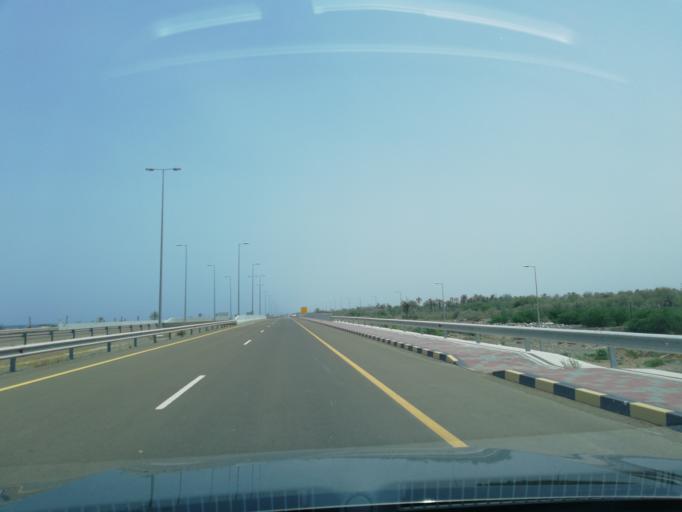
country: OM
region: Al Batinah
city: Al Liwa'
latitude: 24.6388
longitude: 56.5219
